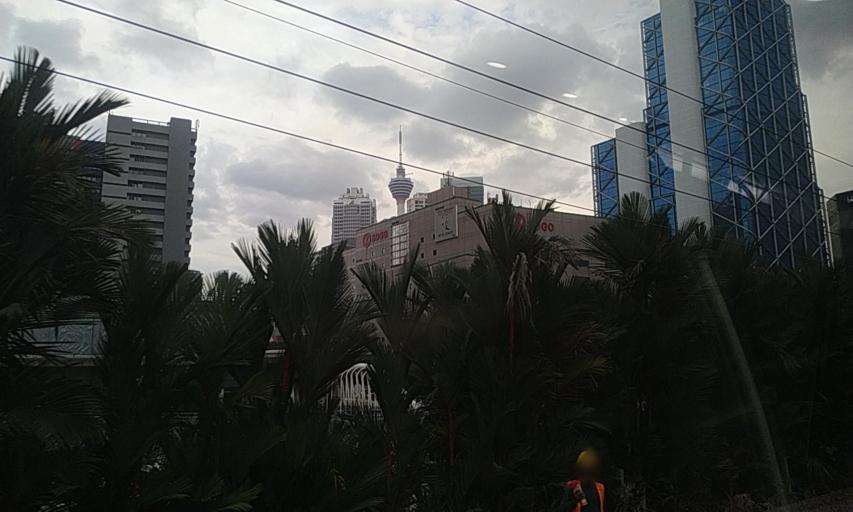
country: MY
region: Kuala Lumpur
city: Kuala Lumpur
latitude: 3.1572
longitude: 101.6937
